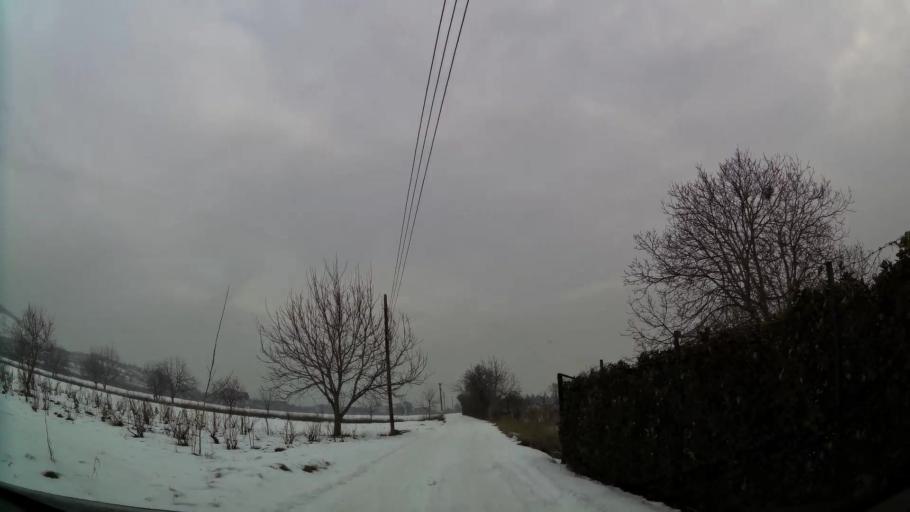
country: MK
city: Kondovo
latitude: 42.0401
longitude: 21.3401
